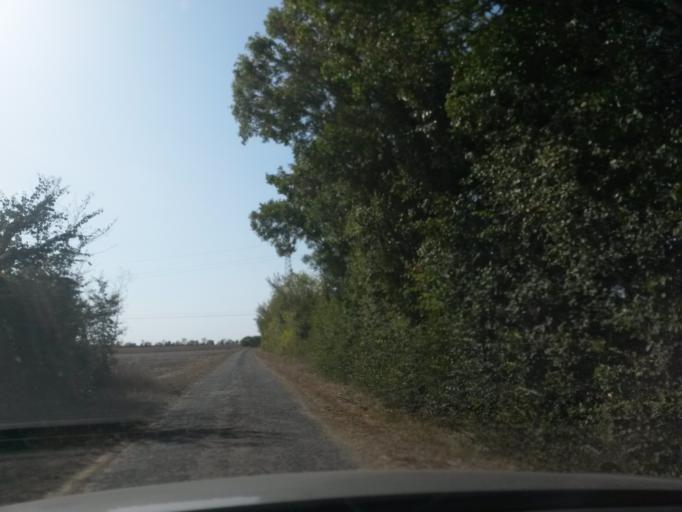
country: FR
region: Poitou-Charentes
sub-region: Departement de la Charente-Maritime
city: Saint-Xandre
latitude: 46.2223
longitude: -1.1083
